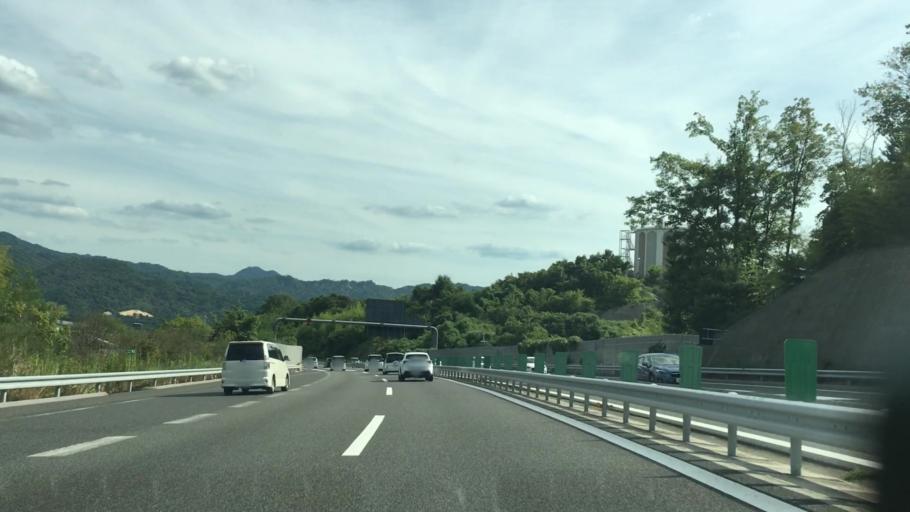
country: JP
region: Shiga Prefecture
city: Kusatsu
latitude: 34.9713
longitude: 135.9604
